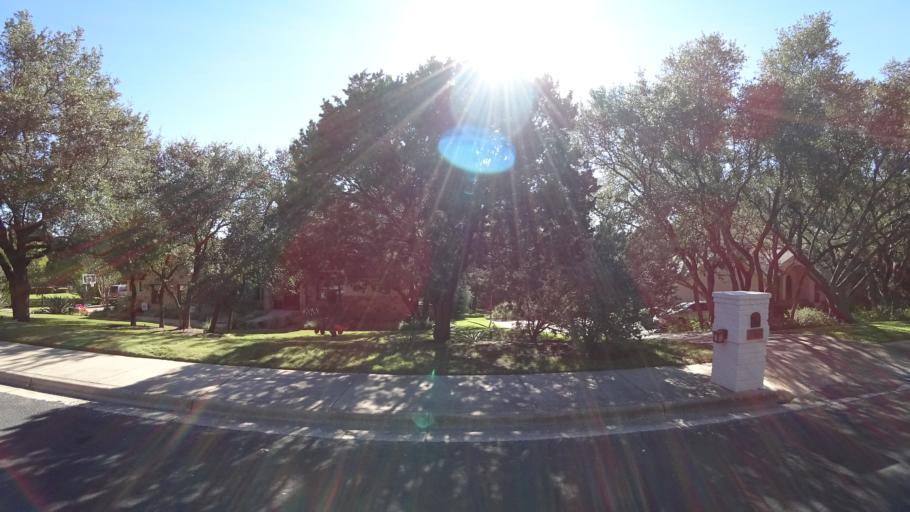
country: US
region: Texas
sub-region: Travis County
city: West Lake Hills
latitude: 30.3307
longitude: -97.7938
